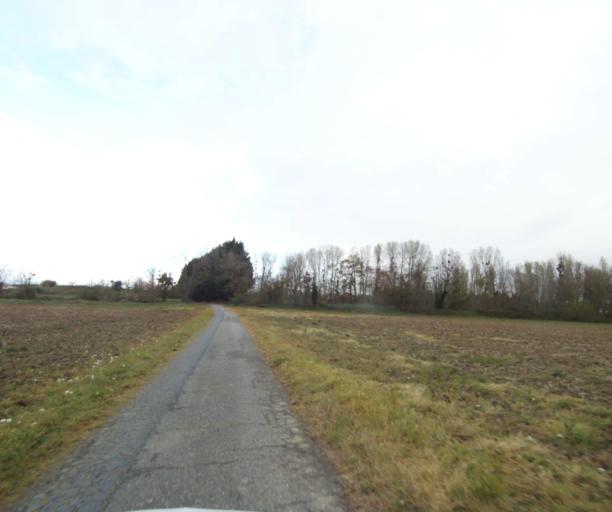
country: FR
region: Midi-Pyrenees
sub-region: Departement de l'Ariege
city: Saverdun
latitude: 43.2254
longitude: 1.5967
